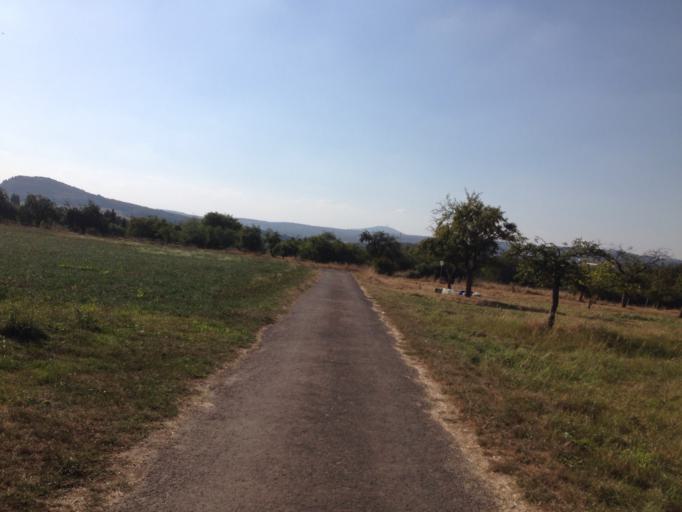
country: DE
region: Hesse
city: Staufenberg
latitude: 50.6529
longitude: 8.7467
